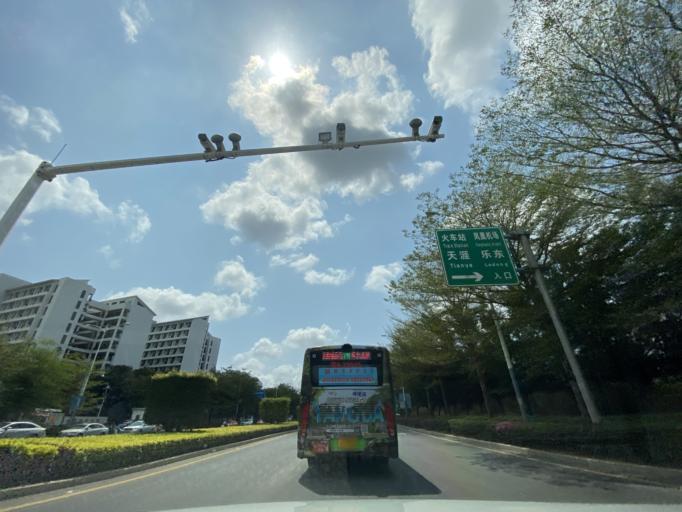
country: CN
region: Hainan
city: Tiandu
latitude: 18.3184
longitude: 109.5261
